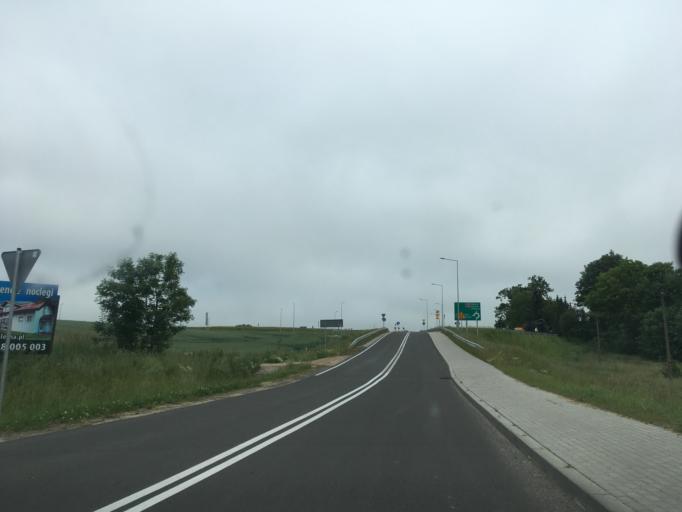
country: PL
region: West Pomeranian Voivodeship
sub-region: Powiat kolobrzeski
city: Ustronie Morskie
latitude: 54.2043
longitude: 15.9086
